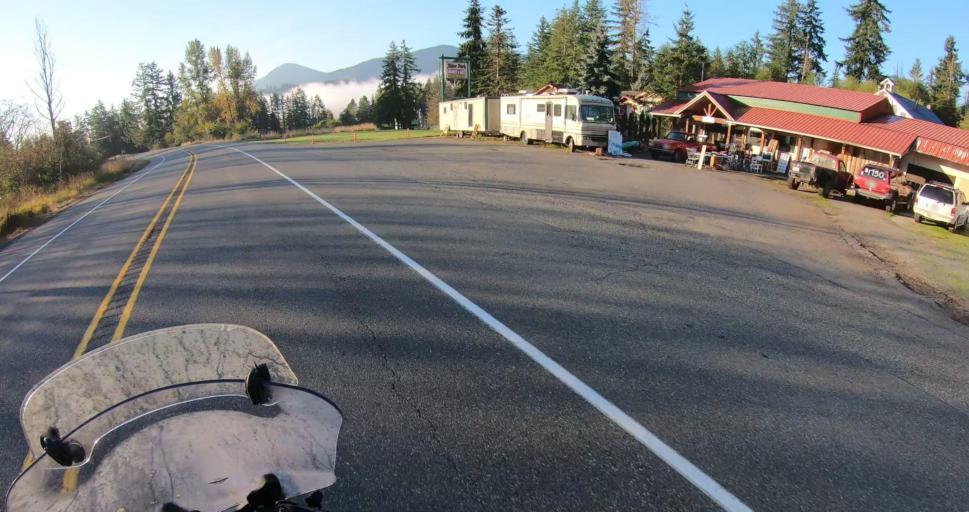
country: US
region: Washington
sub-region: Pierce County
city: Eatonville
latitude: 46.8018
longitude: -122.2920
